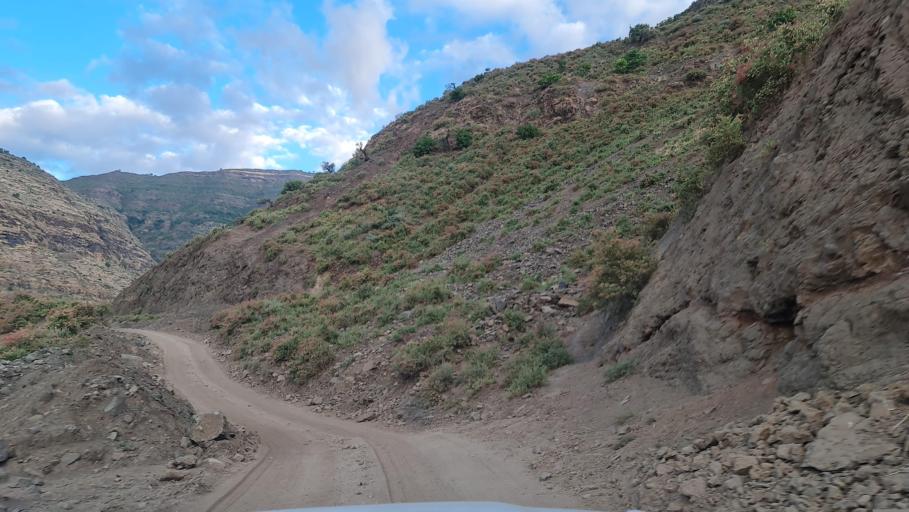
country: ET
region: Amhara
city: Debark'
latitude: 13.0146
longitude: 38.0502
